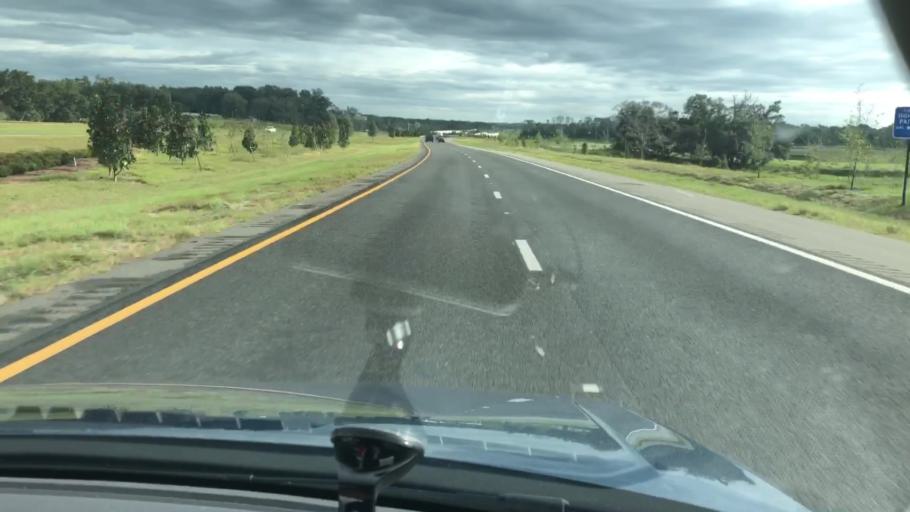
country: US
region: Florida
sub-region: Orange County
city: Zellwood
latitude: 28.7409
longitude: -81.5663
